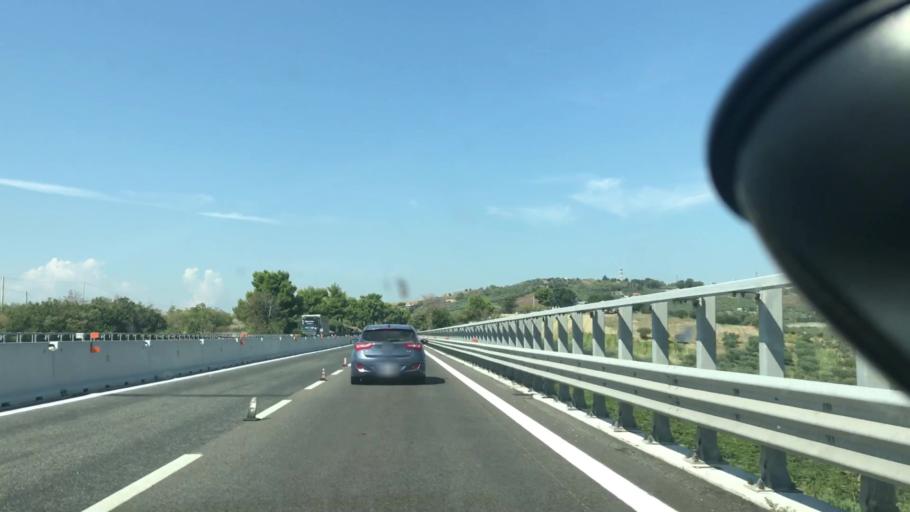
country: IT
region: Abruzzo
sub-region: Provincia di Chieti
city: Marina di Vasto
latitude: 42.0796
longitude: 14.7063
